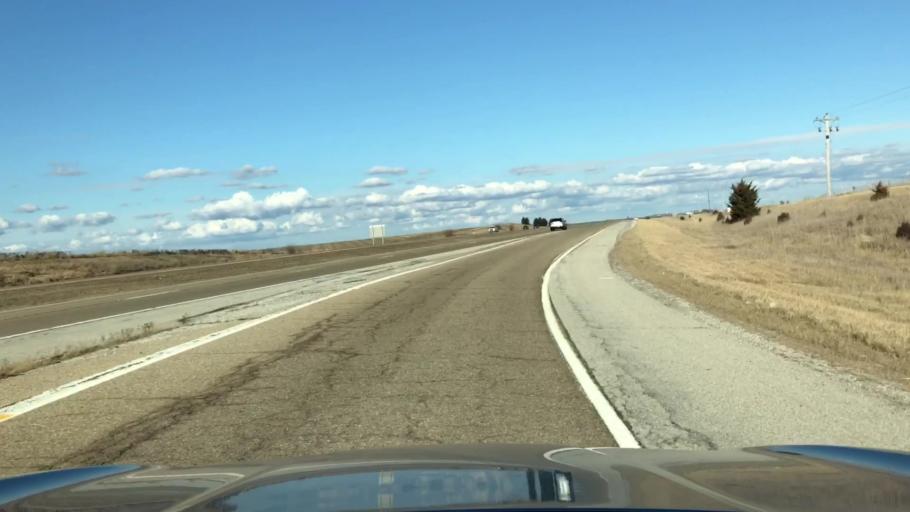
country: US
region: Illinois
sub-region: McLean County
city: Lexington
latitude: 40.6478
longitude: -88.8075
